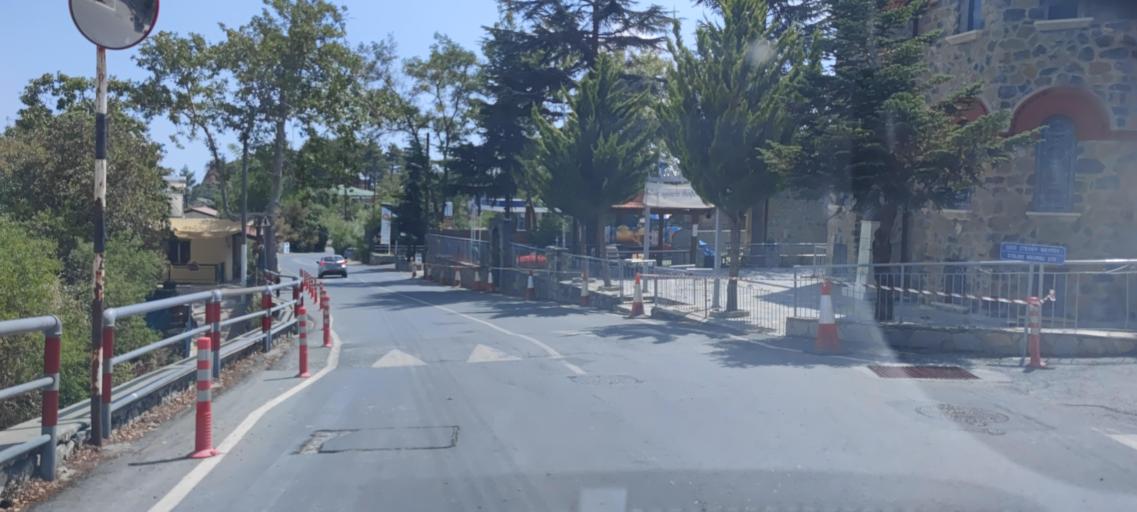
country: CY
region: Limassol
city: Pelendri
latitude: 34.8849
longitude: 32.8634
